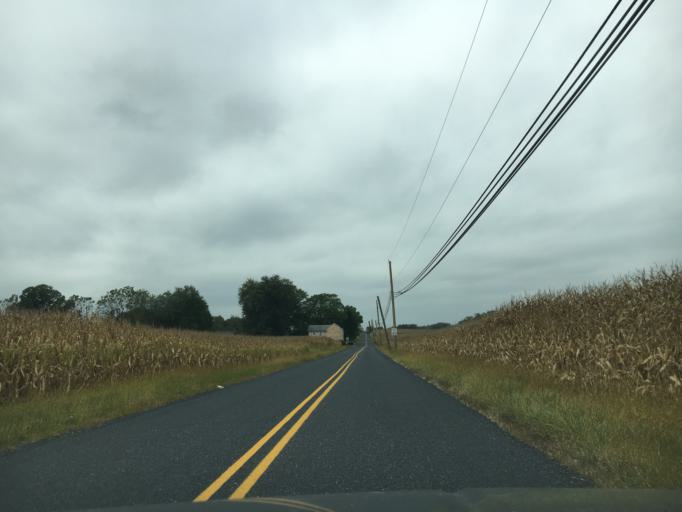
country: US
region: Pennsylvania
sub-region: Northampton County
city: Bath
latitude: 40.6971
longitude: -75.4004
